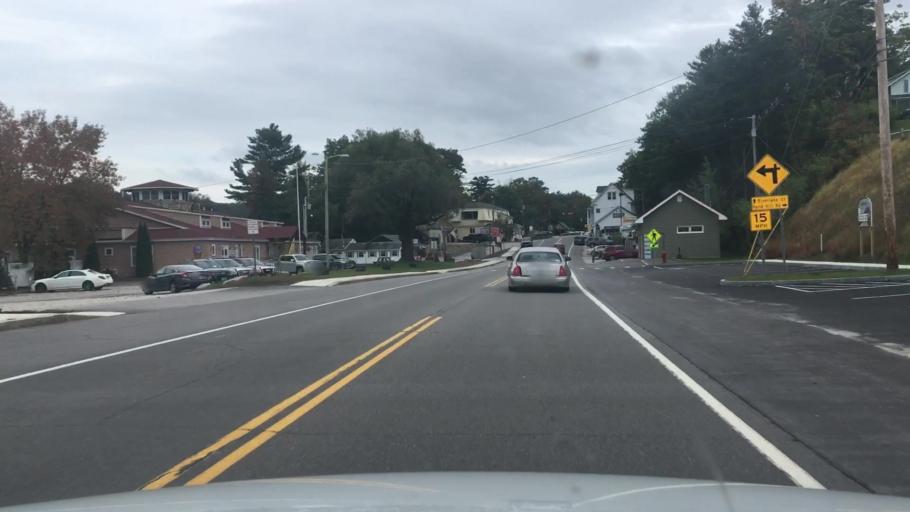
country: US
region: New Hampshire
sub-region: Strafford County
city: New Durham
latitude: 43.4718
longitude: -71.2365
